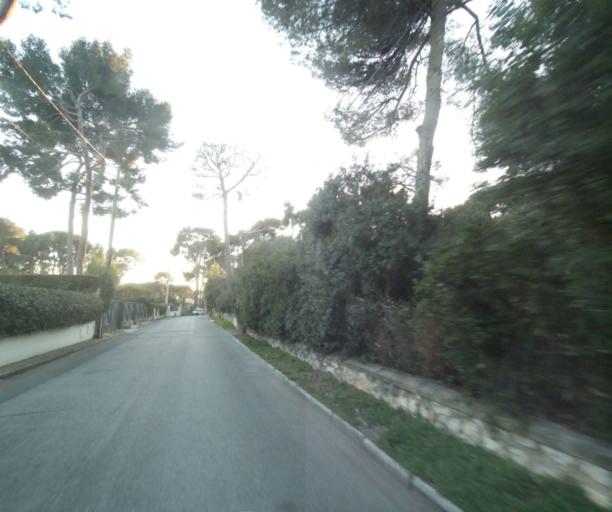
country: FR
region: Provence-Alpes-Cote d'Azur
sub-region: Departement des Alpes-Maritimes
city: Antibes
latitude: 43.5632
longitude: 7.1334
